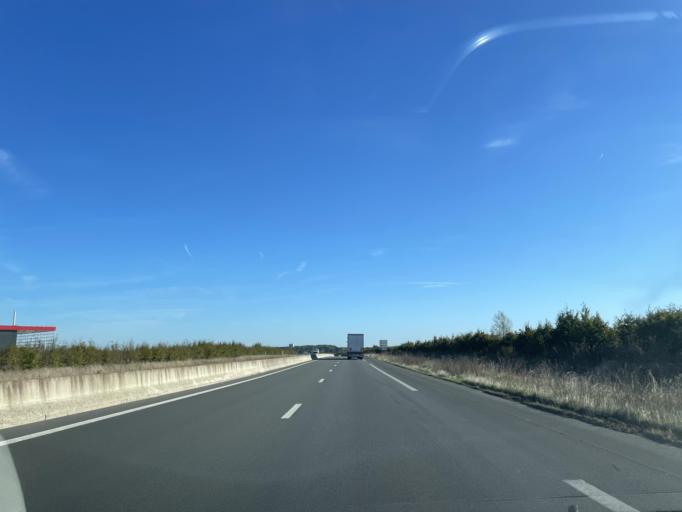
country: FR
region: Picardie
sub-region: Departement de l'Oise
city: Nanteuil-le-Haudouin
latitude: 49.1295
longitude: 2.7935
